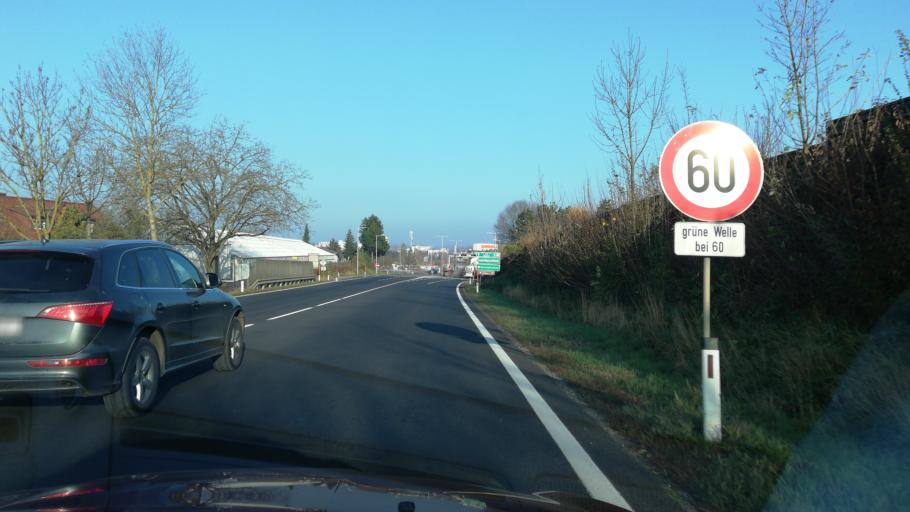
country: AT
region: Upper Austria
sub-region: Wels-Land
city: Thalheim bei Wels
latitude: 48.1493
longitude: 14.0451
